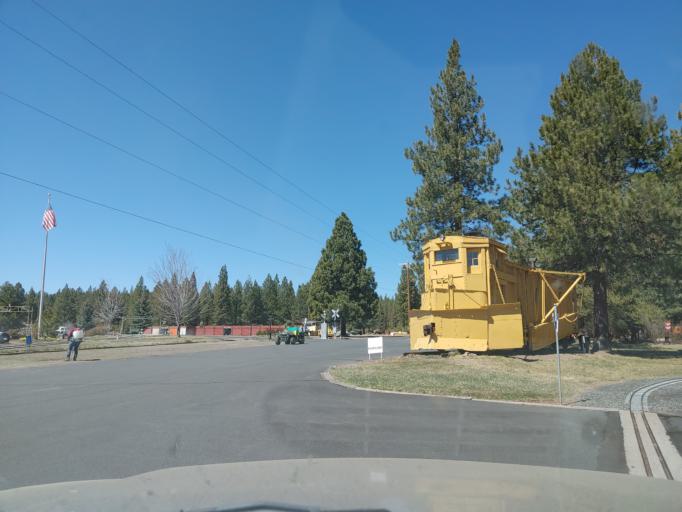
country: US
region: Oregon
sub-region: Klamath County
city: Klamath Falls
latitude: 42.5574
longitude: -121.8868
